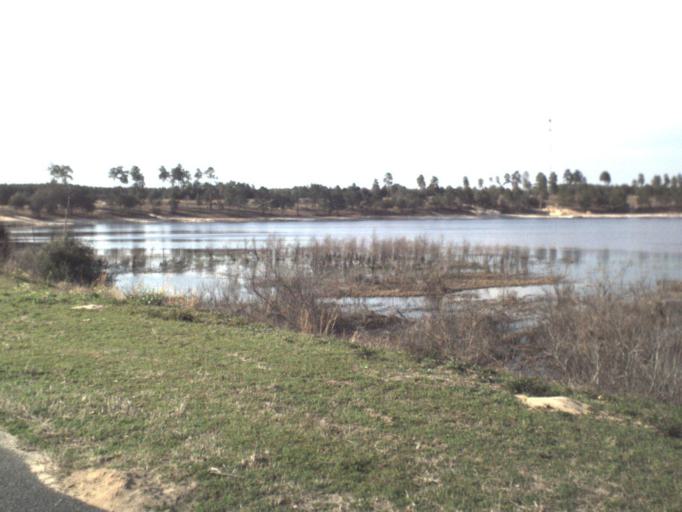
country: US
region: Florida
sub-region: Bay County
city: Lynn Haven
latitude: 30.4299
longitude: -85.6825
